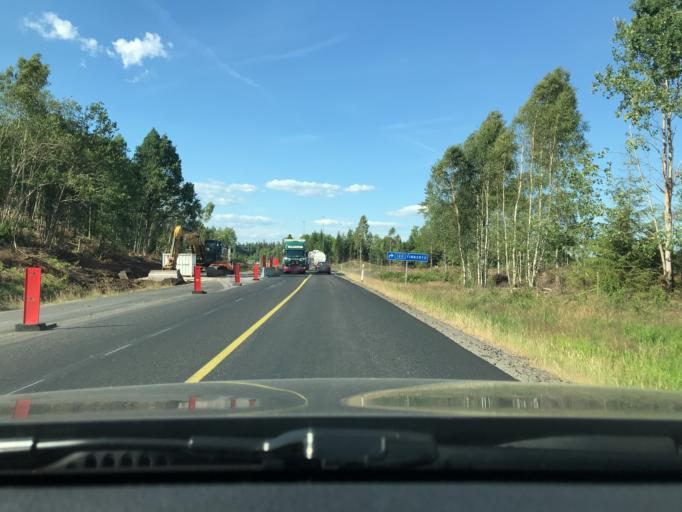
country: SE
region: Kronoberg
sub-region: Almhults Kommun
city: AElmhult
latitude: 56.5602
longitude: 14.1811
